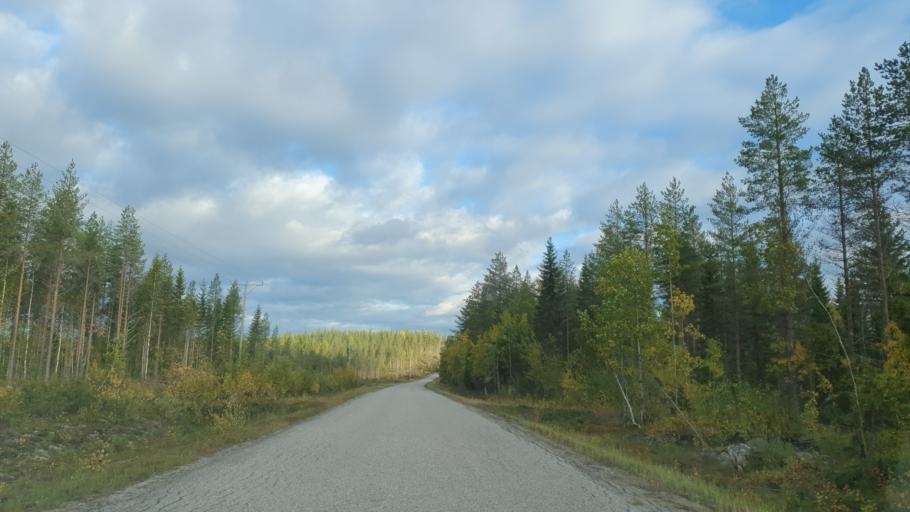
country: FI
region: Kainuu
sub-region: Kehys-Kainuu
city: Kuhmo
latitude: 63.9187
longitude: 30.0608
